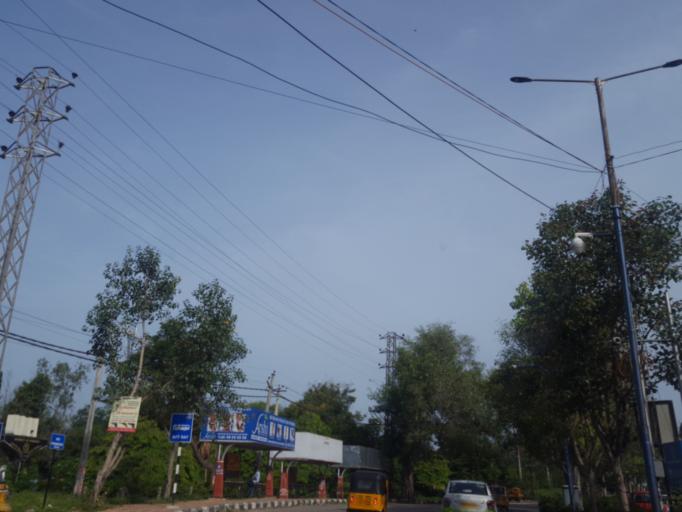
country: IN
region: Telangana
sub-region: Medak
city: Serilingampalle
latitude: 17.4617
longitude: 78.3358
